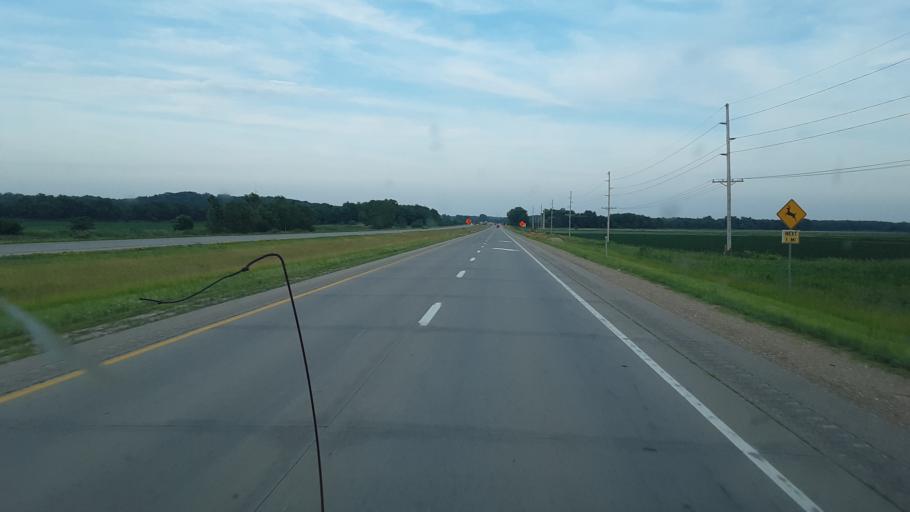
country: US
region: Iowa
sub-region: Tama County
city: Toledo
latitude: 42.0041
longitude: -92.7257
